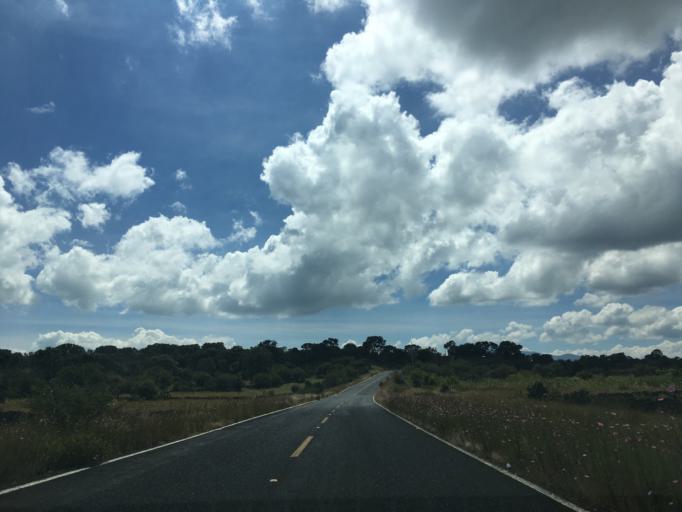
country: MX
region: Michoacan
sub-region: Morelia
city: Cuto de la Esperanza
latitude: 19.7657
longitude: -101.3723
